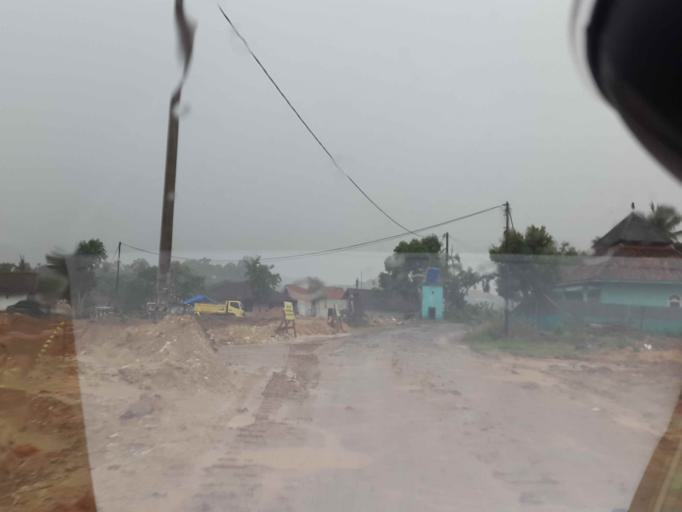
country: ID
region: Lampung
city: Panjang
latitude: -5.3992
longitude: 105.3534
